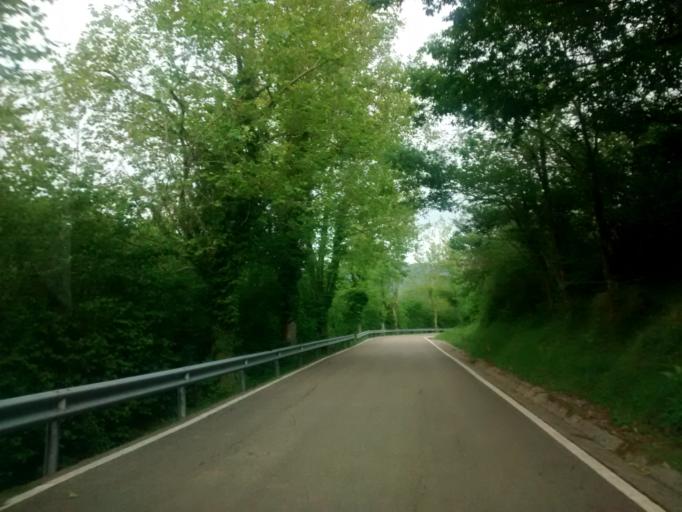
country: ES
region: Cantabria
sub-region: Provincia de Cantabria
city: San Vicente de la Barquera
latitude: 43.2546
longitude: -4.4422
